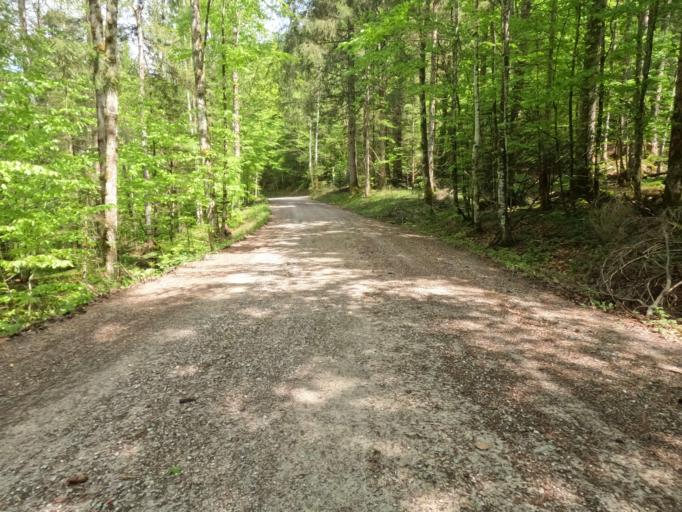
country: DE
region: Bavaria
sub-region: Upper Bavaria
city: Ruhpolding
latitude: 47.7154
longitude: 12.6598
